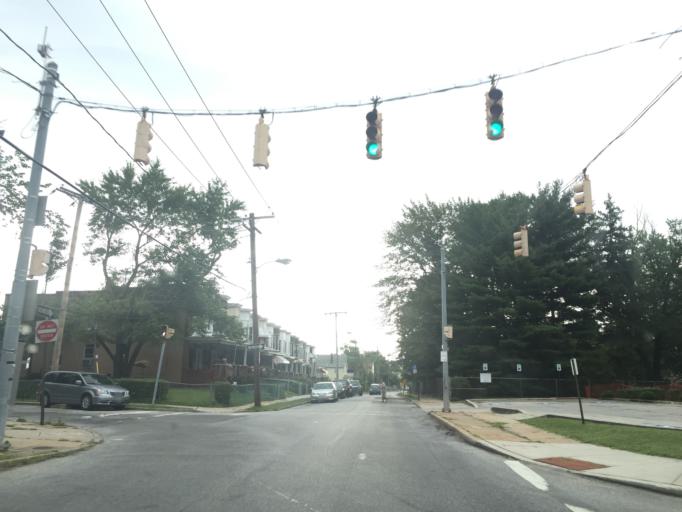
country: US
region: Maryland
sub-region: Baltimore County
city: Charlestown
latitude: 39.2841
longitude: -76.6811
